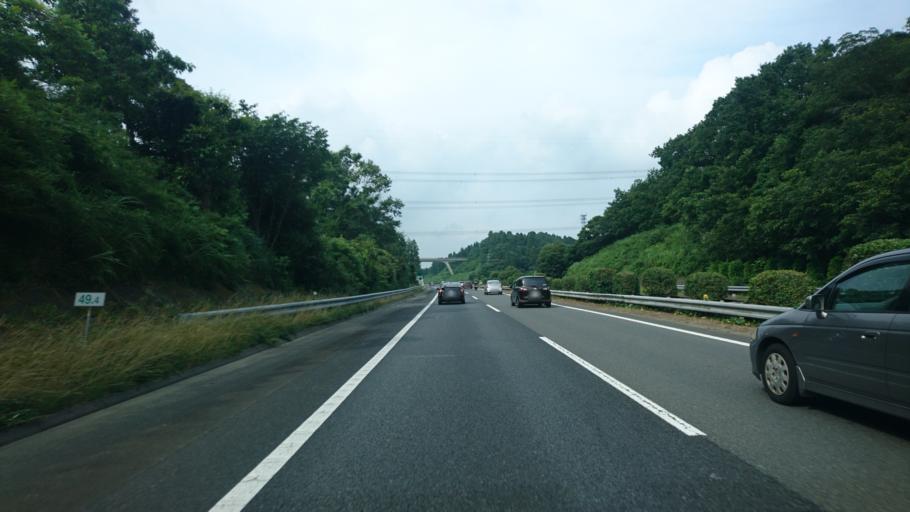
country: JP
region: Chiba
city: Ichihara
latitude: 35.4501
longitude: 140.0787
